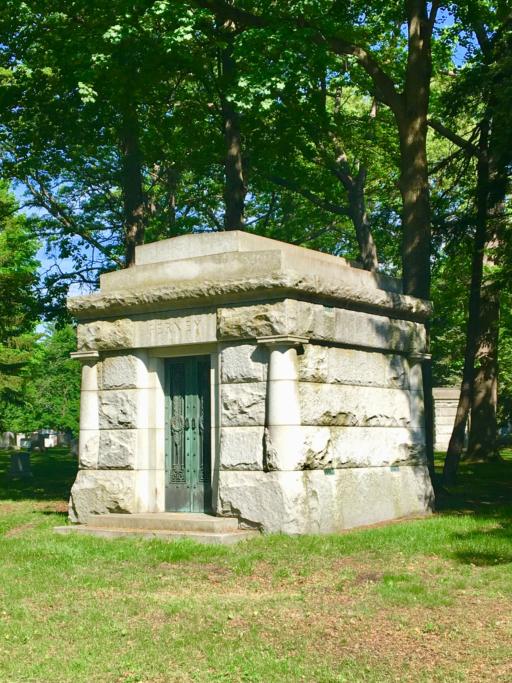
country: US
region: Michigan
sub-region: Oakland County
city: Ferndale
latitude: 42.4412
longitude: -83.1270
